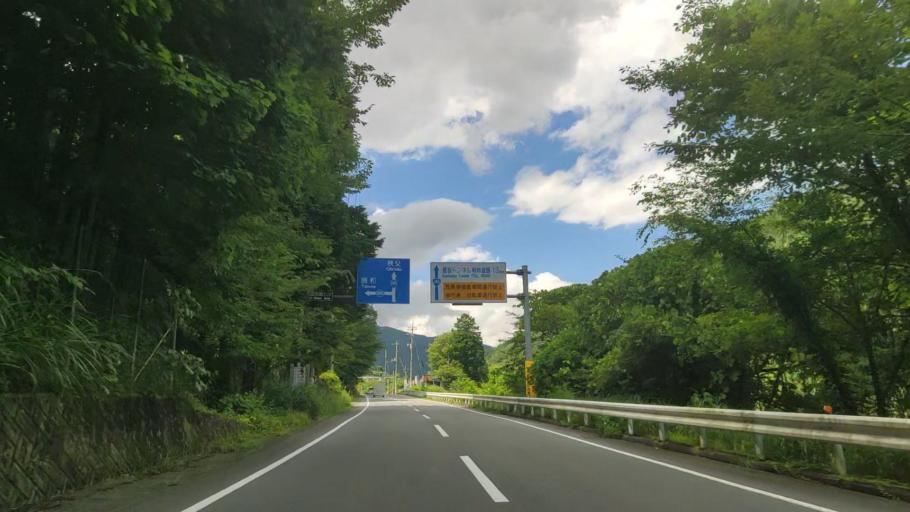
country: JP
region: Yamanashi
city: Enzan
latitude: 35.7759
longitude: 138.7388
